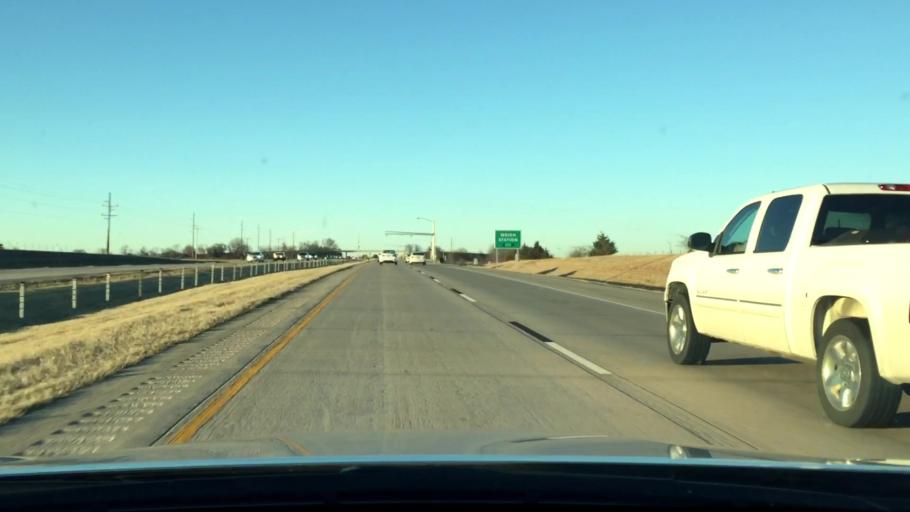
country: US
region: Oklahoma
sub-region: Love County
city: Marietta
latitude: 33.8907
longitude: -97.1344
